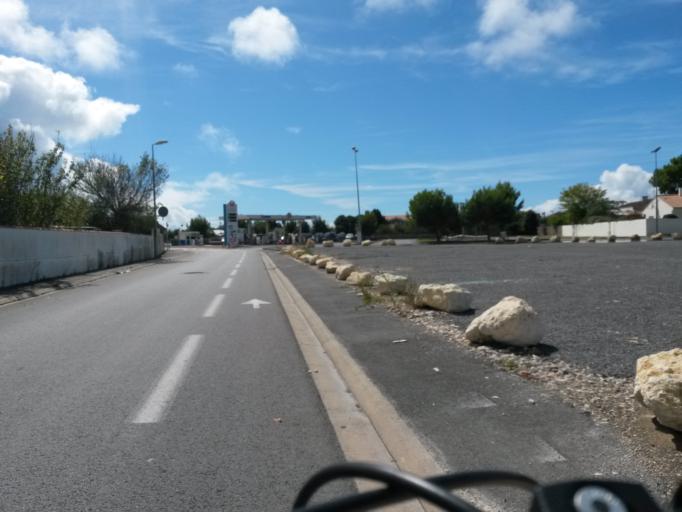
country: FR
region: Poitou-Charentes
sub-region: Departement de la Charente-Maritime
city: Dolus-d'Oleron
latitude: 45.9402
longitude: -1.3060
